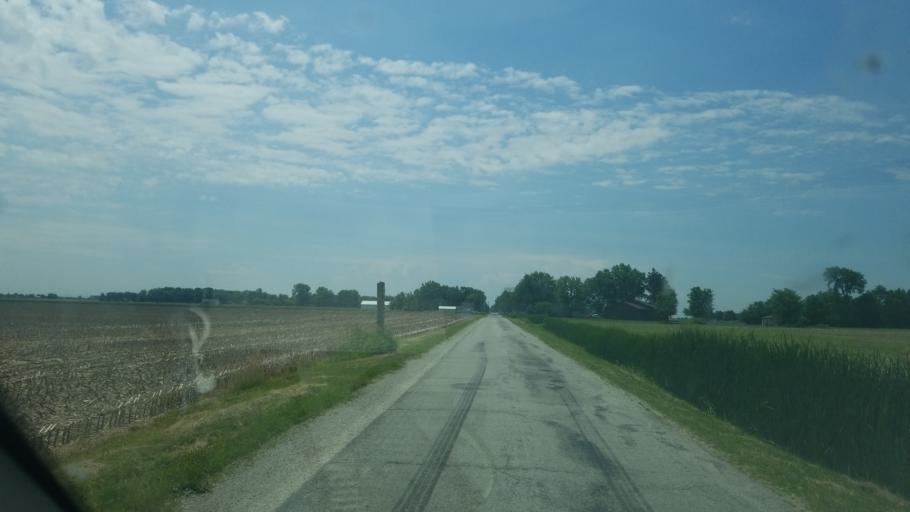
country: US
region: Ohio
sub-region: Wood County
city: North Baltimore
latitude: 41.2469
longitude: -83.6212
